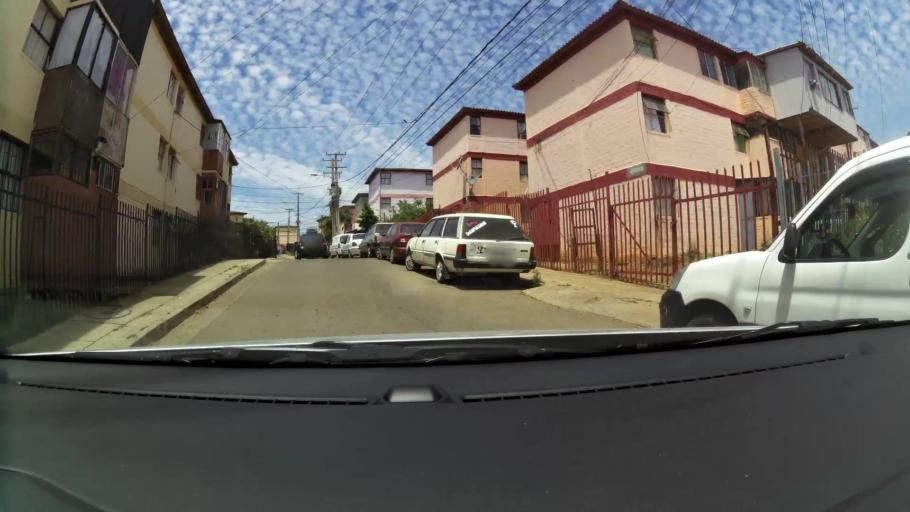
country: CL
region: Valparaiso
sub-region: Provincia de Valparaiso
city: Vina del Mar
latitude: -33.0568
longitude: -71.5630
